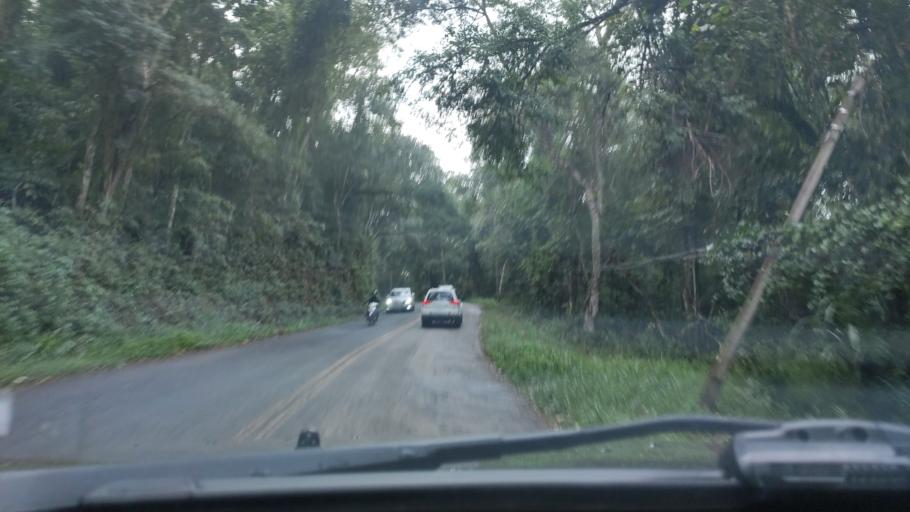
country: BR
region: Sao Paulo
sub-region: Jarinu
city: Jarinu
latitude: -23.1194
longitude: -46.7580
